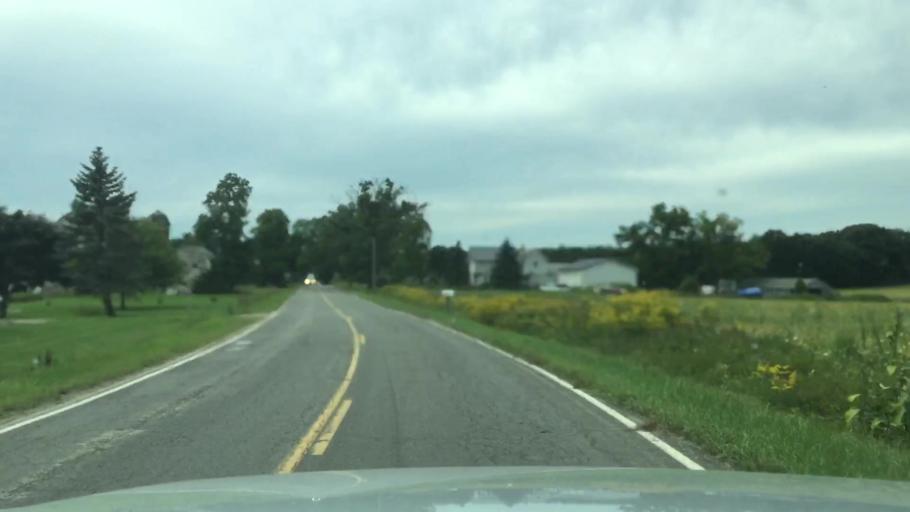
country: US
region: Michigan
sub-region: Shiawassee County
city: Corunna
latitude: 42.9340
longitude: -84.0861
